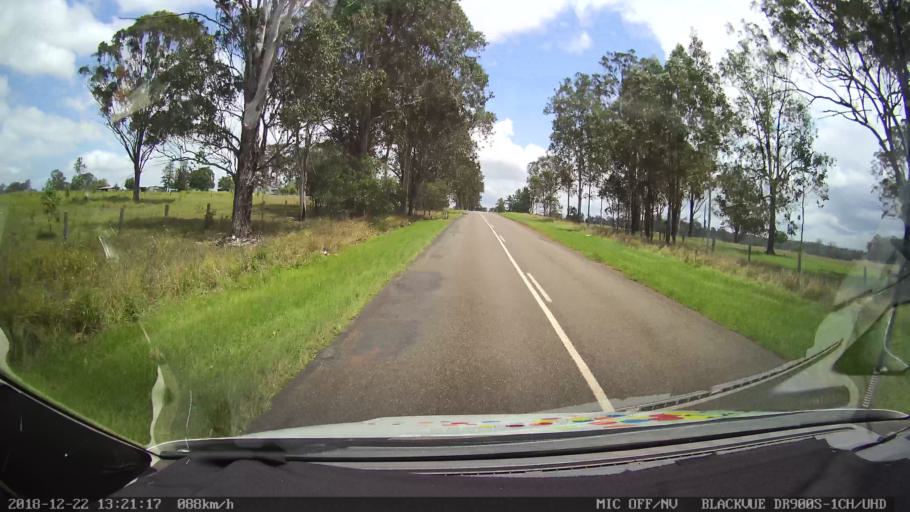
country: AU
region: New South Wales
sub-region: Clarence Valley
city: Coutts Crossing
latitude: -29.7753
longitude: 152.9217
